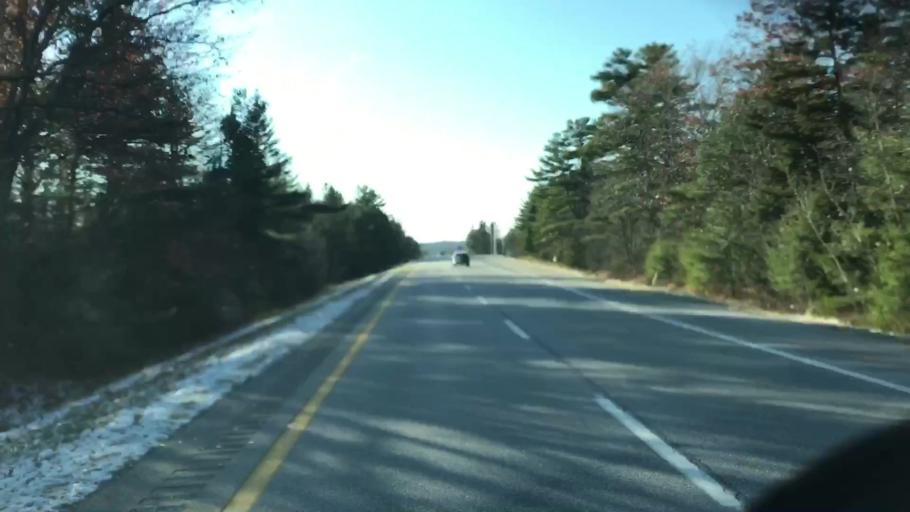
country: US
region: Maine
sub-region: Penobscot County
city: Hampden
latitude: 44.7678
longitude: -68.8803
